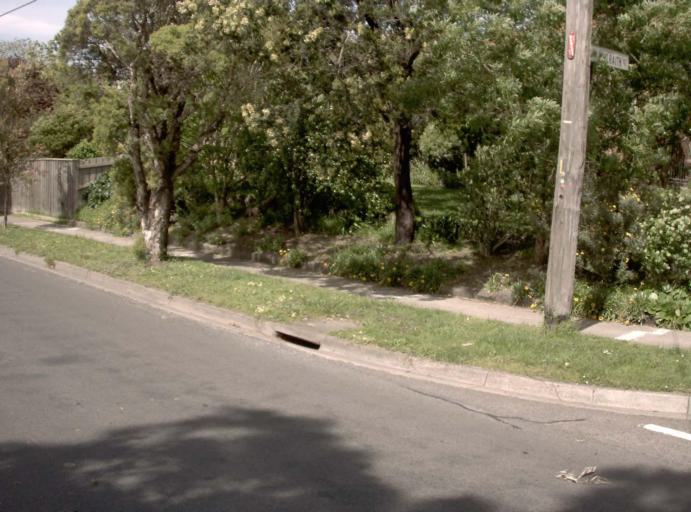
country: AU
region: Victoria
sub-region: Maroondah
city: Croydon North
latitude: -37.7914
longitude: 145.3061
